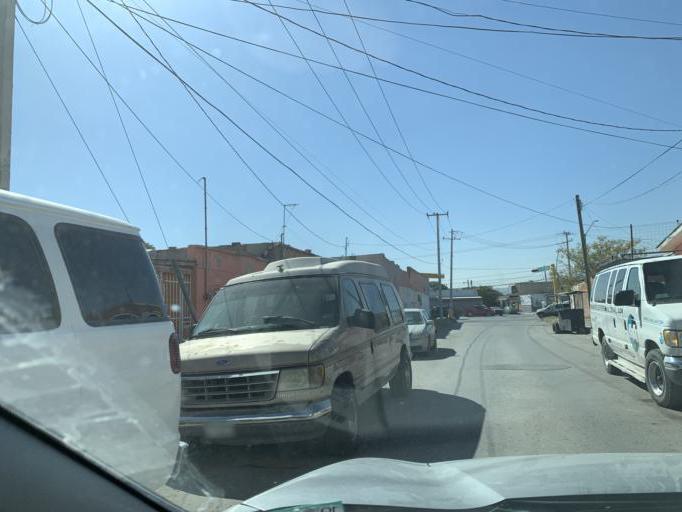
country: MX
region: Chihuahua
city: Ciudad Juarez
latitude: 31.7210
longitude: -106.4641
